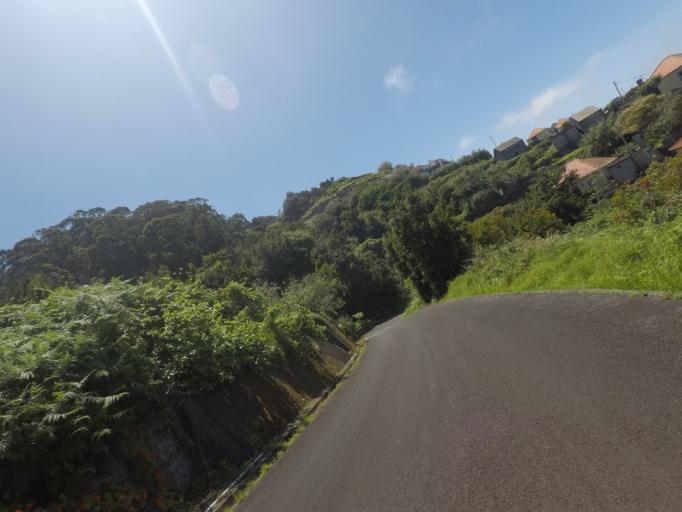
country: PT
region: Madeira
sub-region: Porto Moniz
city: Porto Moniz
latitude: 32.8448
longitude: -17.1516
